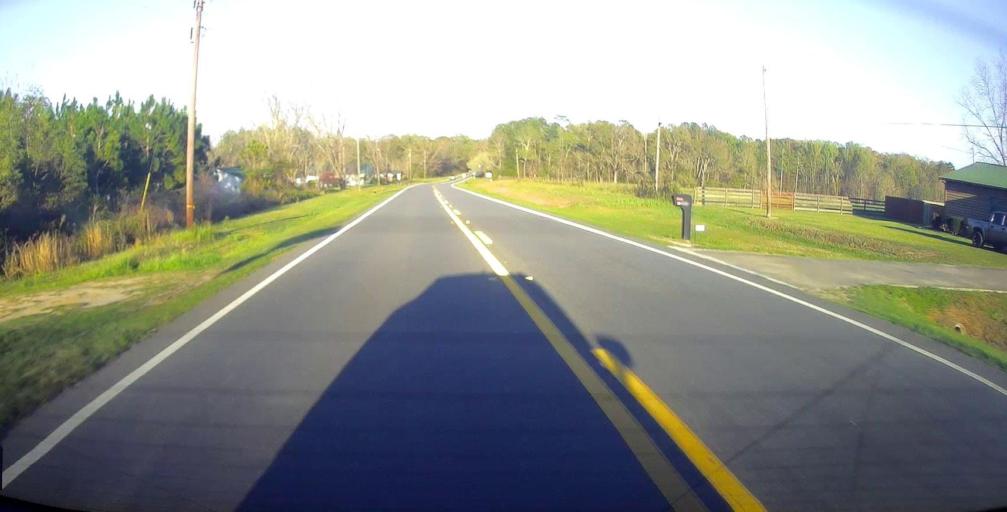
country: US
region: Georgia
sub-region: Wilcox County
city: Abbeville
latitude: 31.9915
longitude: -83.3209
